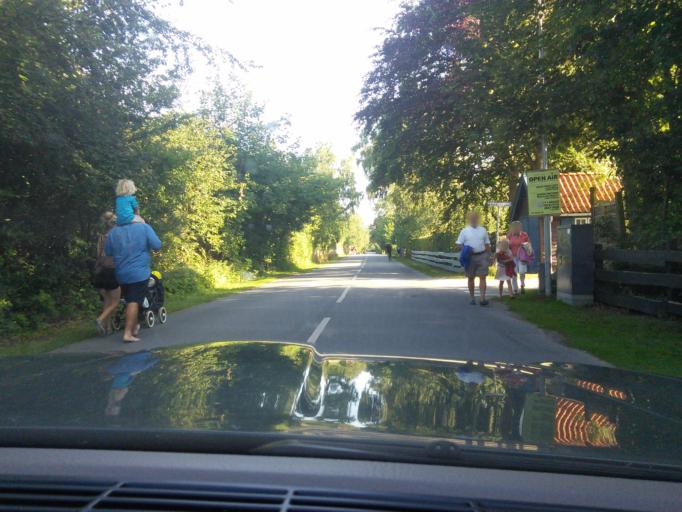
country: DK
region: Capital Region
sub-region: Halsnaes Kommune
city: Liseleje
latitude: 56.0102
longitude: 11.9642
